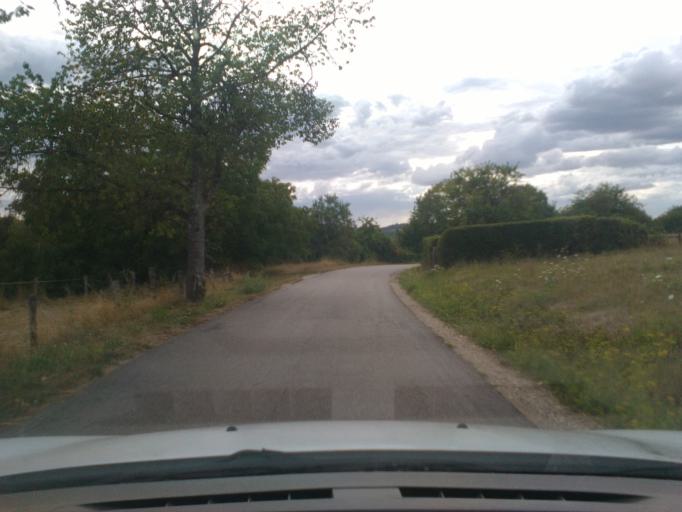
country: FR
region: Lorraine
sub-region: Departement des Vosges
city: Portieux
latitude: 48.3382
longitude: 6.3518
